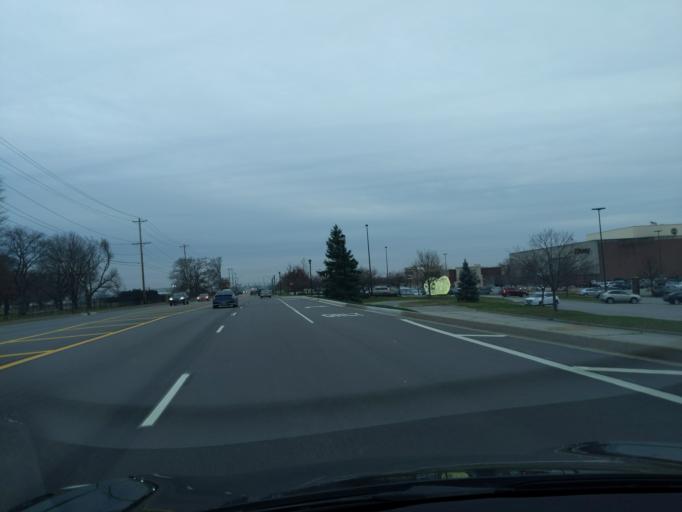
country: US
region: Indiana
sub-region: Saint Joseph County
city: Georgetown
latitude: 41.7227
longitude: -86.1879
